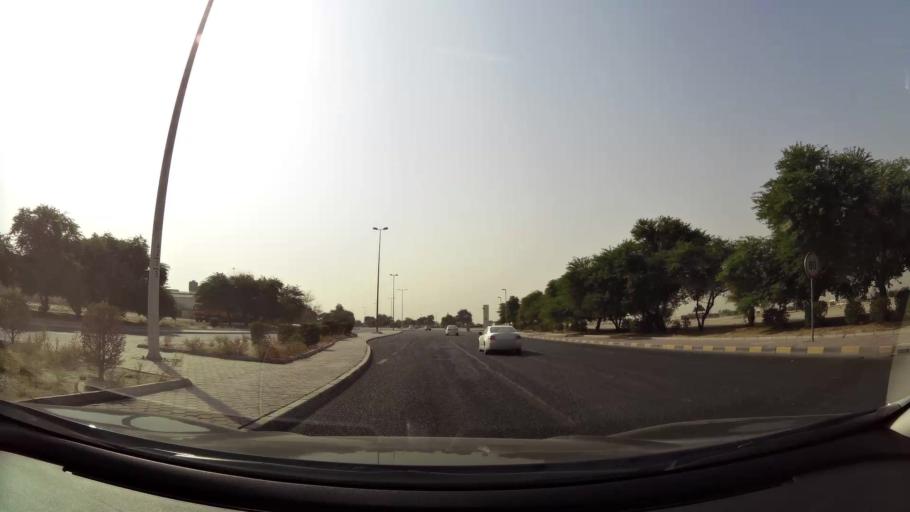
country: KW
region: Al Asimah
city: Ar Rabiyah
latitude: 29.2887
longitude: 47.8319
